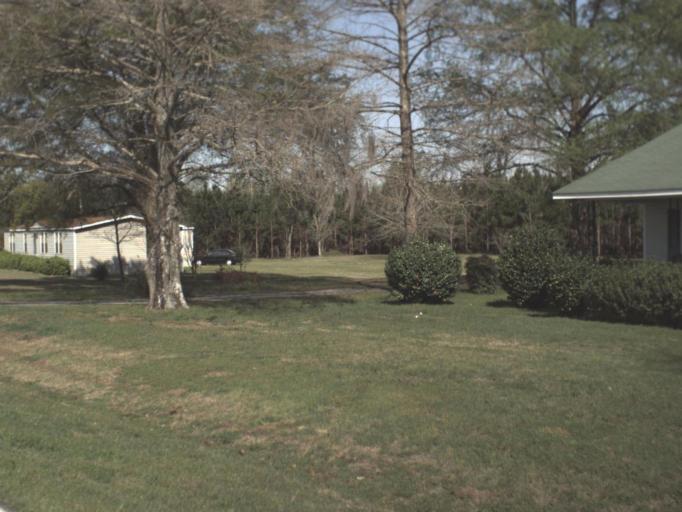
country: US
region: Florida
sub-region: Jackson County
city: Graceville
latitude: 30.9531
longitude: -85.4377
